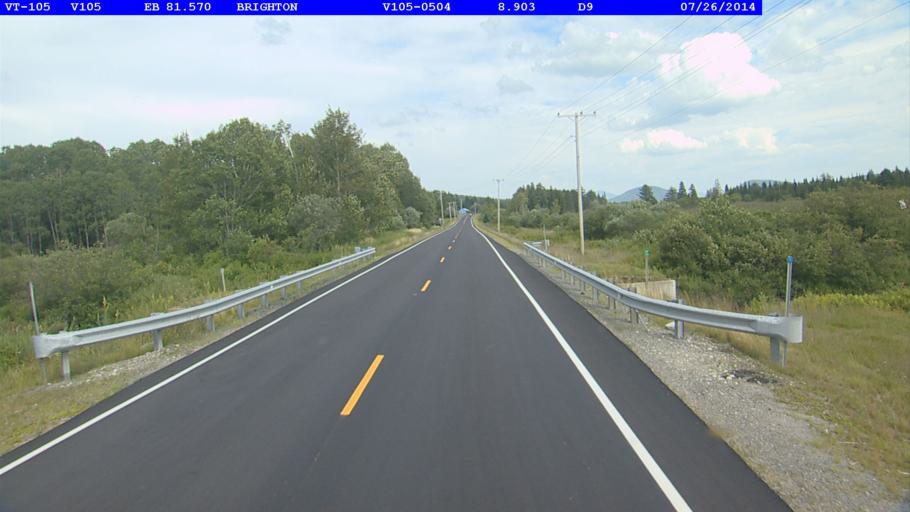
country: US
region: New Hampshire
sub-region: Coos County
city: Stratford
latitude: 44.7861
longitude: -71.8092
